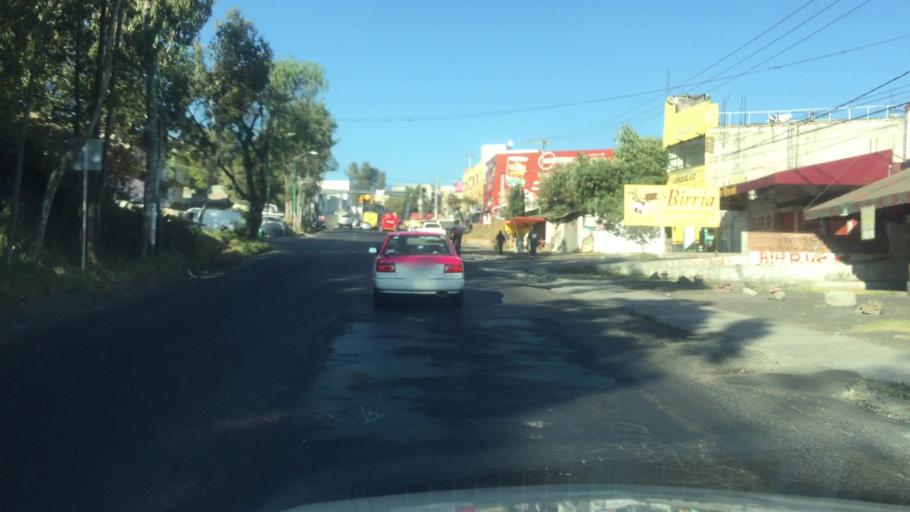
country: MX
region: Mexico City
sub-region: Tlalpan
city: Lomas de Tepemecatl
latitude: 19.2676
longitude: -99.2097
